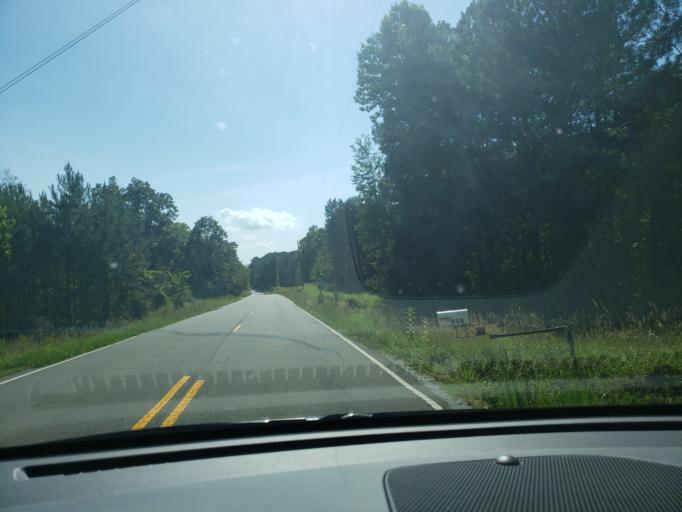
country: US
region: North Carolina
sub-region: Durham County
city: Gorman
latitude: 36.1258
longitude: -78.8861
